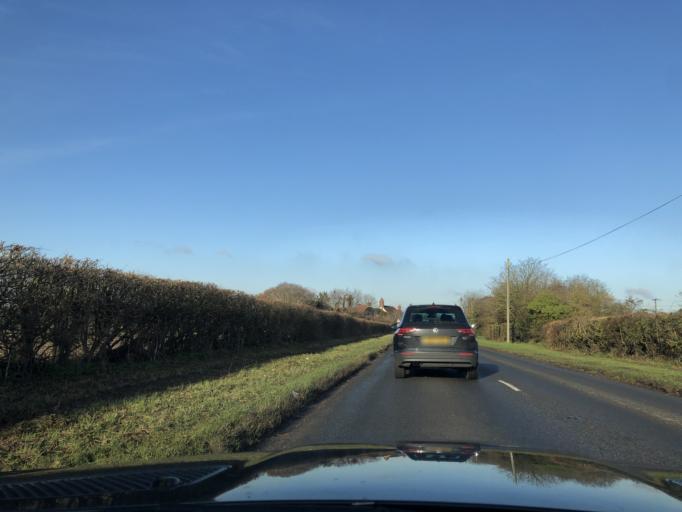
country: GB
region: England
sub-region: Buckinghamshire
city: High Wycombe
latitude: 51.6070
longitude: -0.7708
